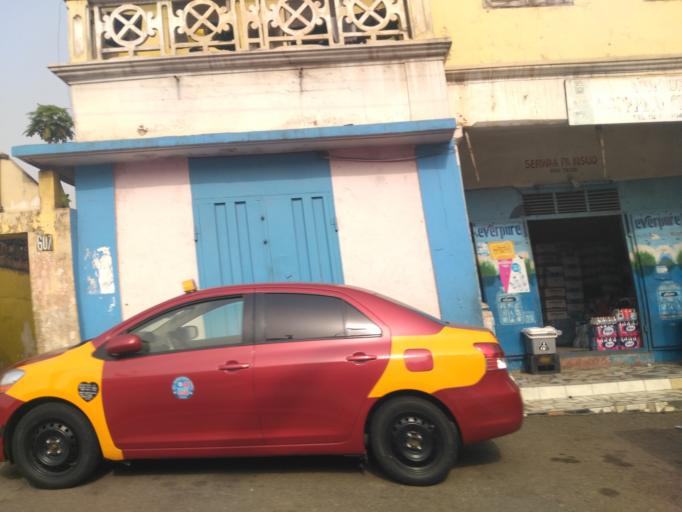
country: GH
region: Ashanti
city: Kumasi
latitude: 6.6845
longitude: -1.6111
